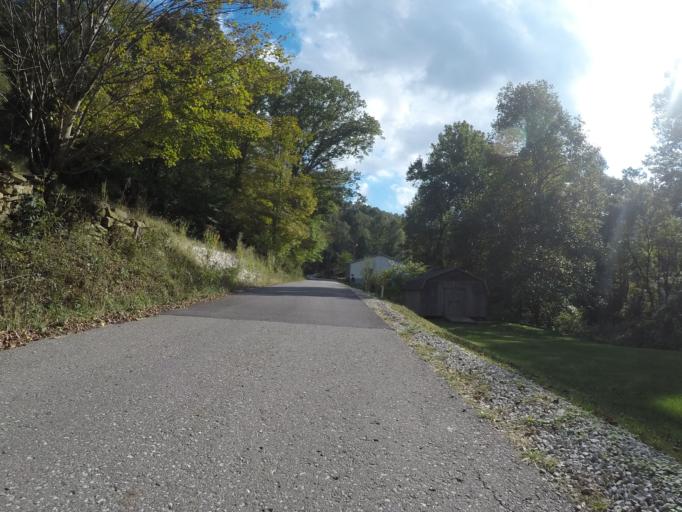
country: US
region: West Virginia
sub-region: Wayne County
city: Lavalette
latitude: 38.3616
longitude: -82.4852
